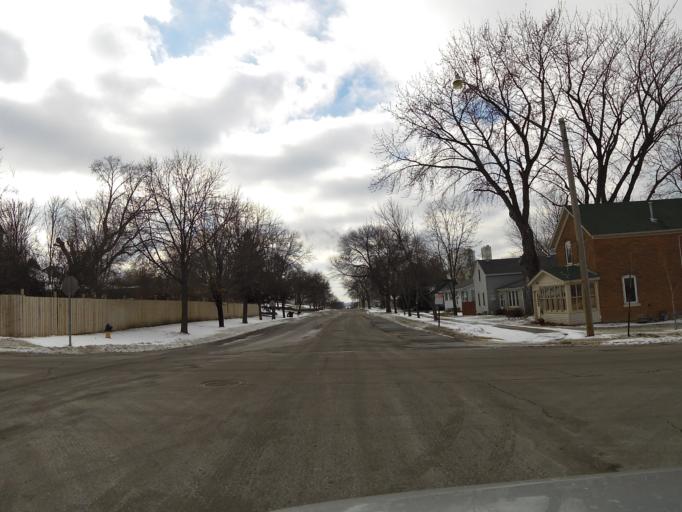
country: US
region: Minnesota
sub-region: Scott County
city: Shakopee
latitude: 44.7961
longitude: -93.5305
